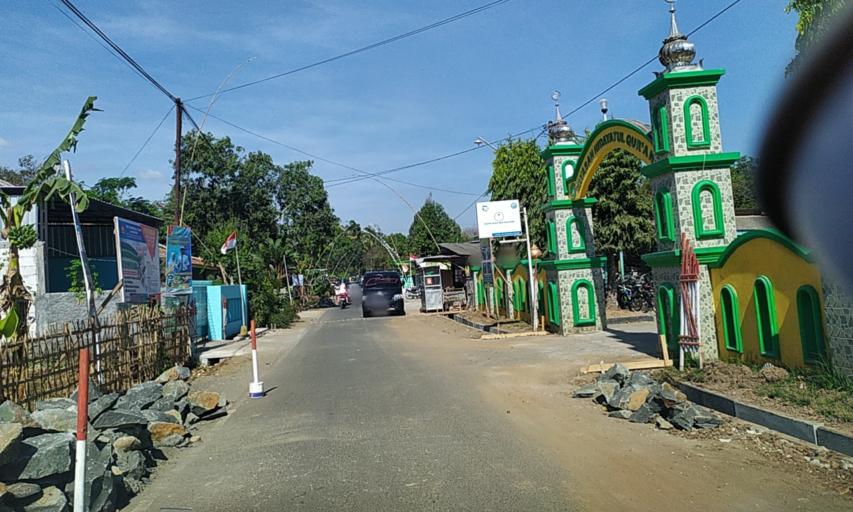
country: ID
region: Central Java
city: Kroya
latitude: -7.6304
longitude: 109.2609
